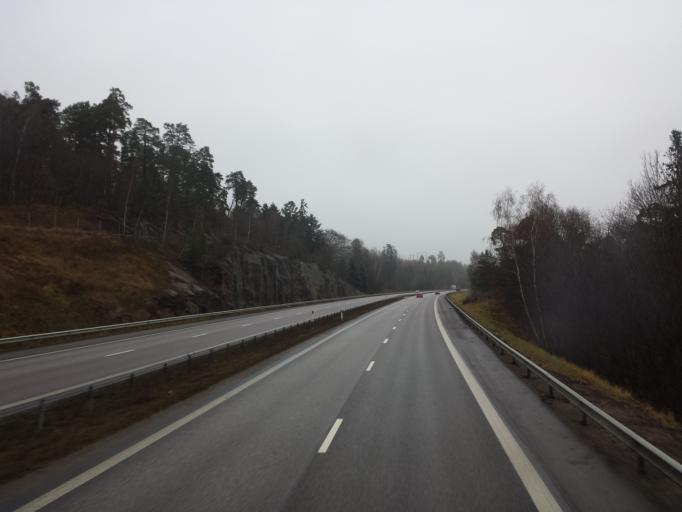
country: SE
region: OEstergoetland
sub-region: Norrkopings Kommun
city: Jursla
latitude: 58.6667
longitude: 16.2069
